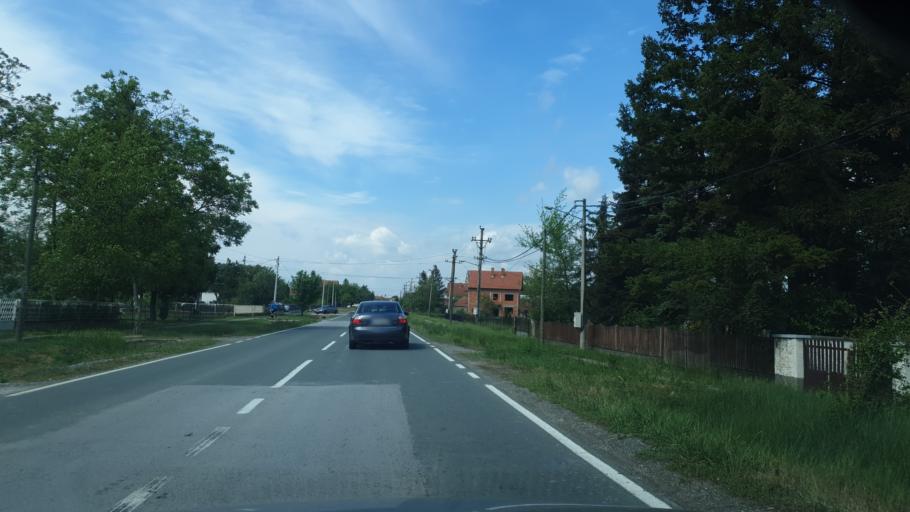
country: RS
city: Stubline
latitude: 44.5631
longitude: 20.1480
